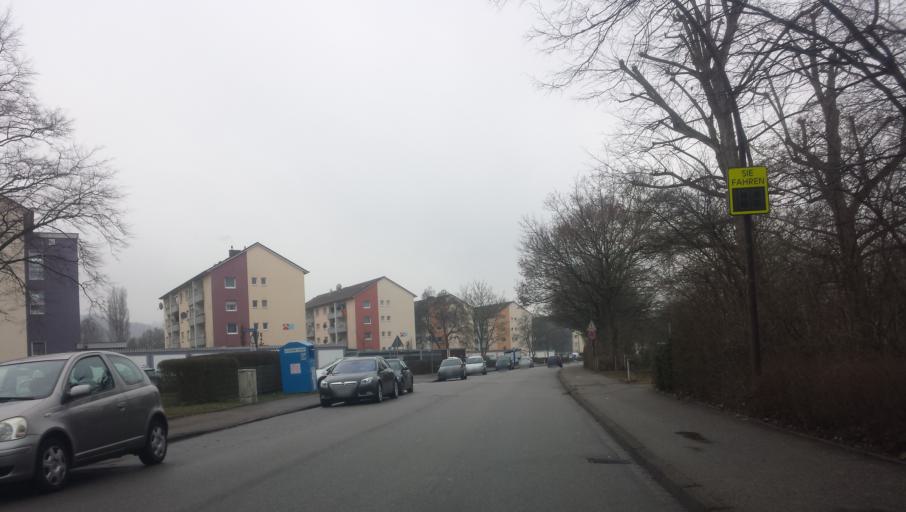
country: DE
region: Baden-Wuerttemberg
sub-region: Karlsruhe Region
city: Bruchsal
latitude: 49.1154
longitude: 8.5746
